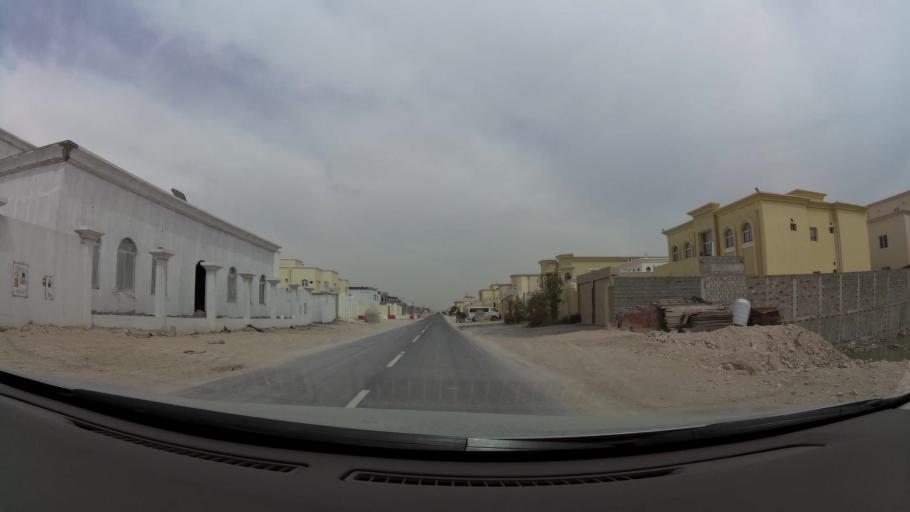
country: QA
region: Baladiyat ar Rayyan
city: Ar Rayyan
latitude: 25.2161
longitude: 51.4644
